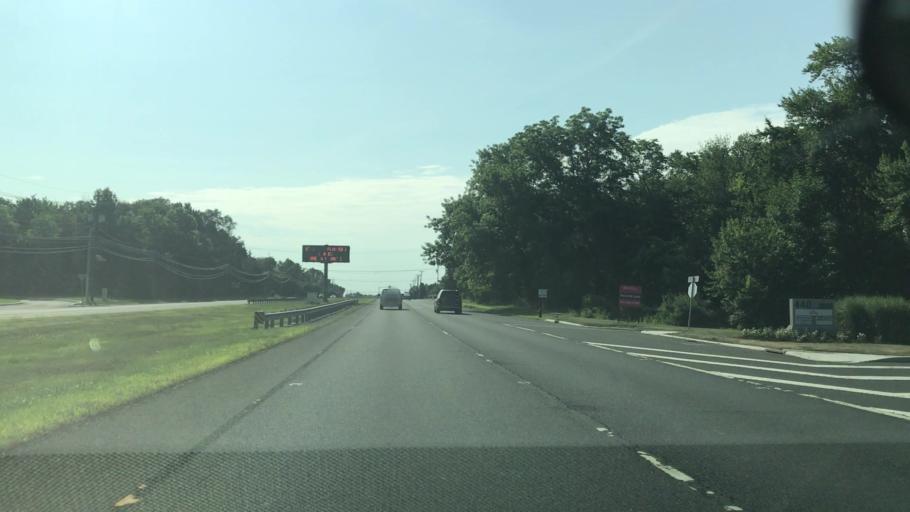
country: US
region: New Jersey
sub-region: Somerset County
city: Bridgewater
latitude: 40.5909
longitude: -74.6487
